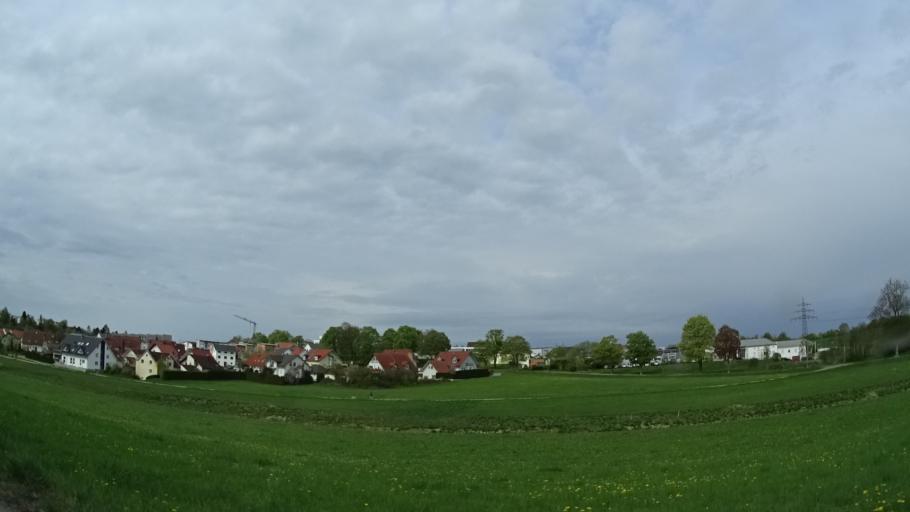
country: DE
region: Baden-Wuerttemberg
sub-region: Freiburg Region
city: Villingen-Schwenningen
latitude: 48.0724
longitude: 8.4736
